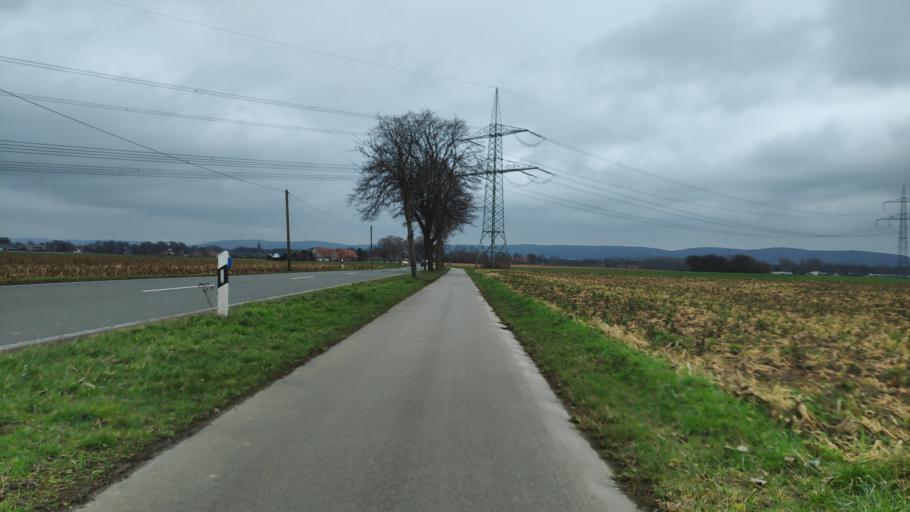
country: DE
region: North Rhine-Westphalia
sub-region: Regierungsbezirk Detmold
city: Hille
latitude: 52.3245
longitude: 8.8107
